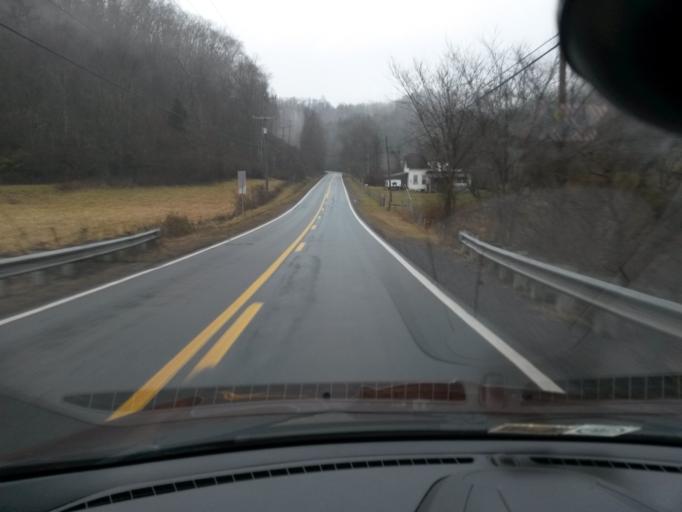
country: US
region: West Virginia
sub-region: Greenbrier County
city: Lewisburg
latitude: 37.8705
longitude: -80.4901
